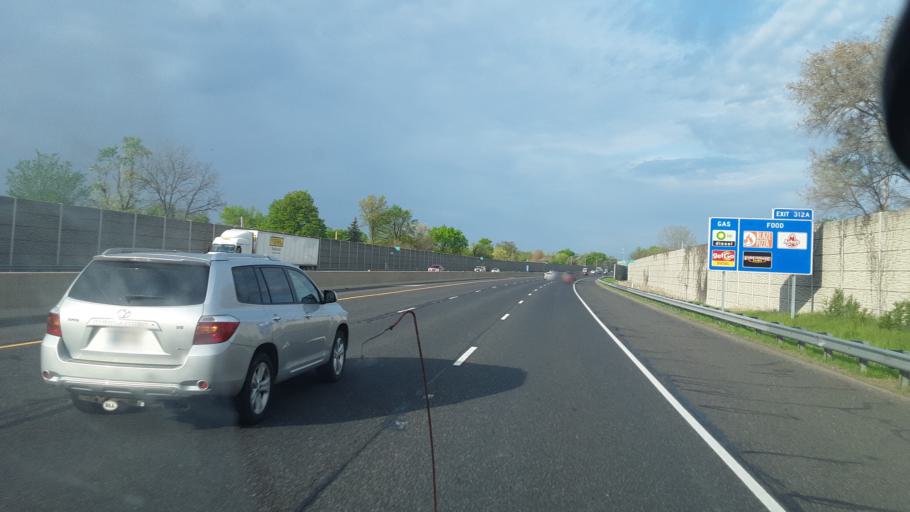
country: US
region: Indiana
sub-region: Allen County
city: Fort Wayne
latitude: 41.1460
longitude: -85.1197
